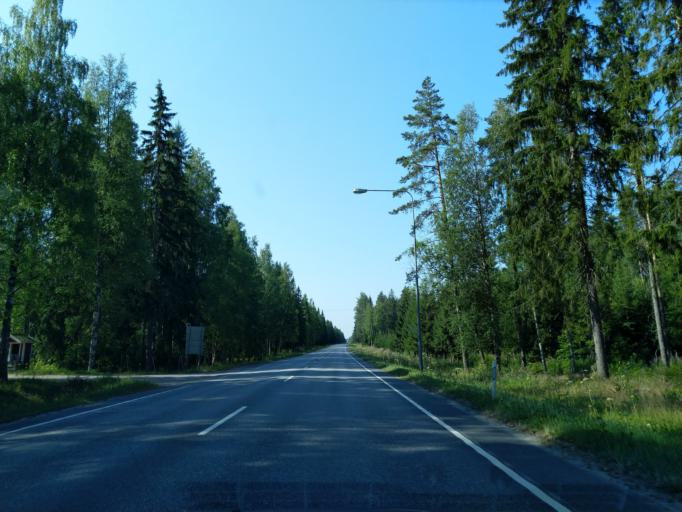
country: FI
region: Satakunta
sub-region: Pori
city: Pomarkku
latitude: 61.6580
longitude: 21.9664
